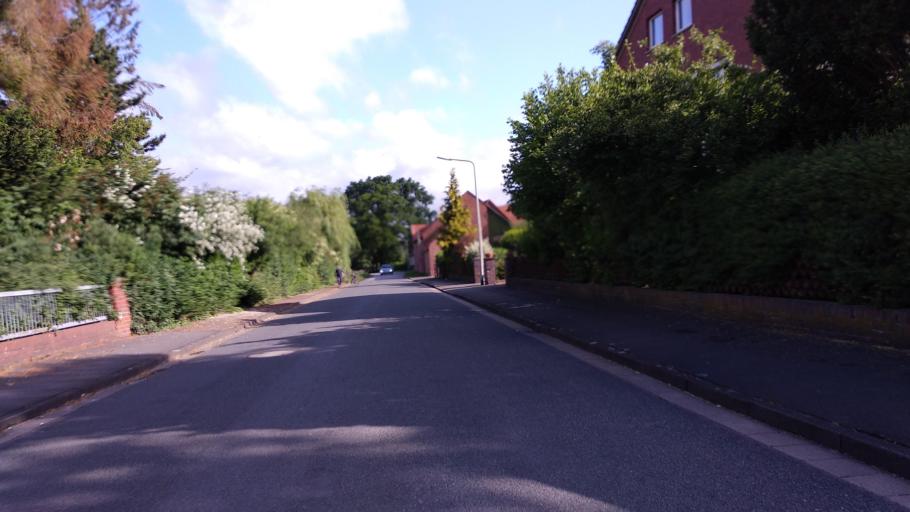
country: DE
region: Lower Saxony
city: Hagenburg
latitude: 52.4605
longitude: 9.3814
